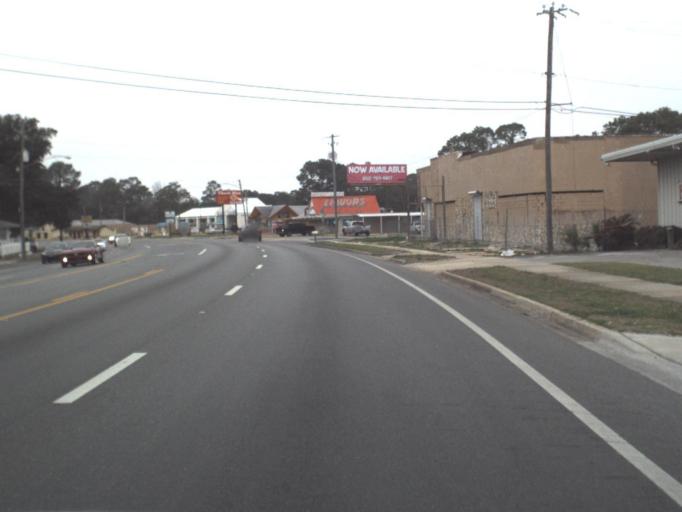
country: US
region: Florida
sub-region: Bay County
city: Pretty Bayou
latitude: 30.1796
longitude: -85.7027
